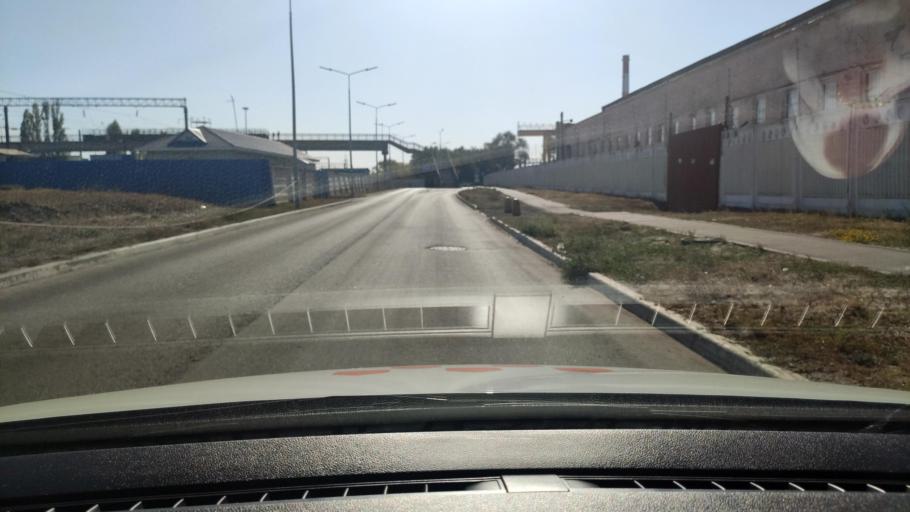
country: RU
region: Voronezj
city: Voronezh
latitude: 51.6376
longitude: 39.2568
